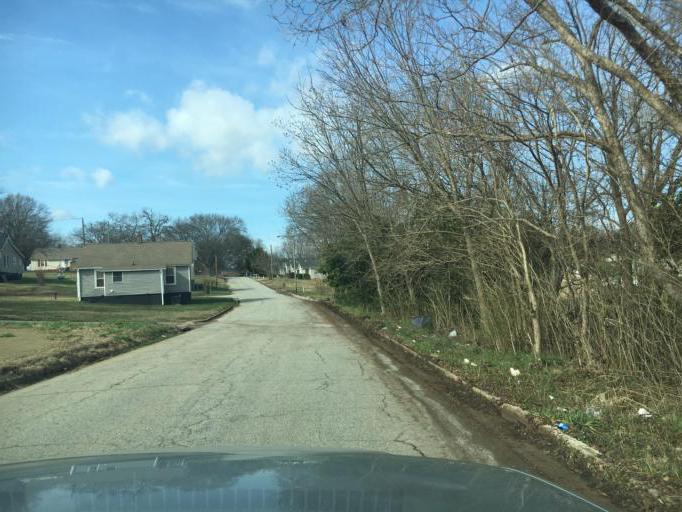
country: US
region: South Carolina
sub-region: Spartanburg County
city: Inman
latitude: 35.0387
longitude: -82.0929
